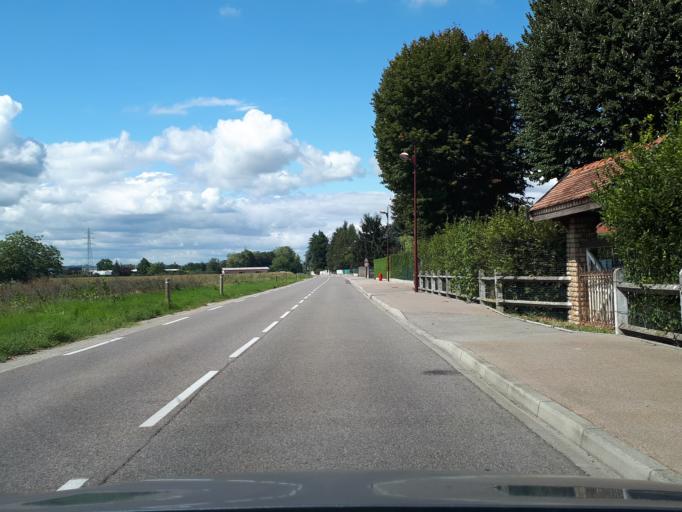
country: FR
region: Rhone-Alpes
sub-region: Departement de l'Isere
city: Ruy
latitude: 45.5899
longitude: 5.3040
